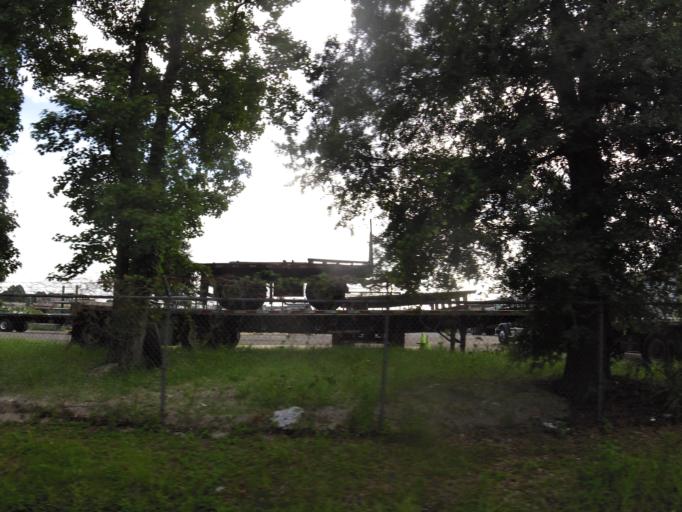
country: US
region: Florida
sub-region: Duval County
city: Jacksonville
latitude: 30.3639
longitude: -81.7095
